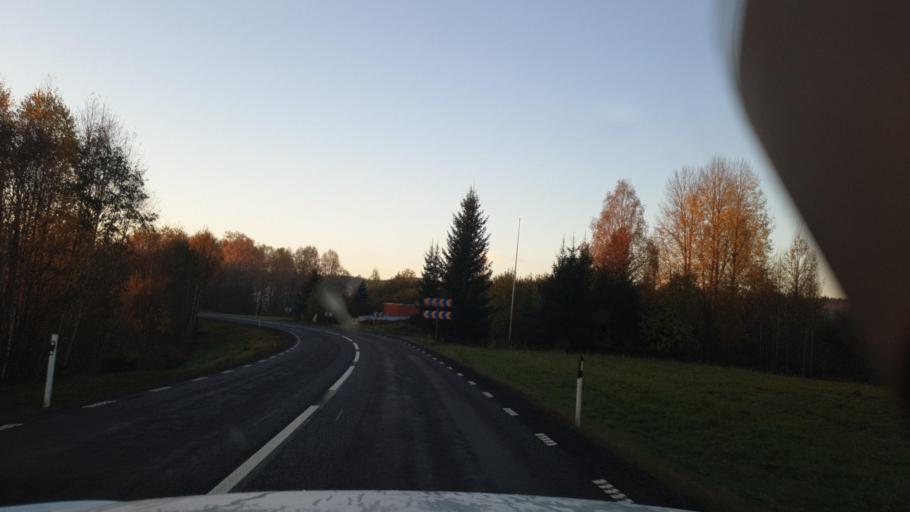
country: SE
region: Vaermland
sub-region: Eda Kommun
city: Charlottenberg
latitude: 59.8302
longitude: 12.3154
